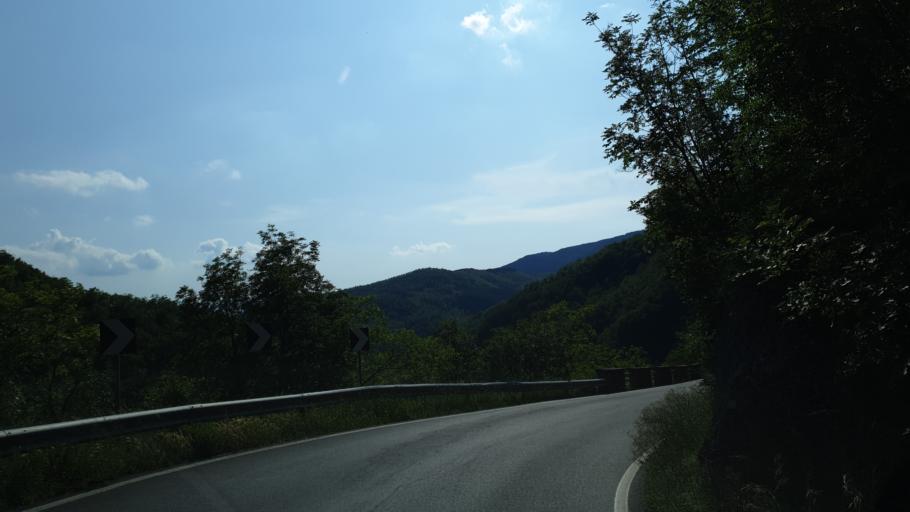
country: IT
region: Tuscany
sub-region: Province of Arezzo
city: Soci
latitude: 43.7712
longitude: 11.8527
